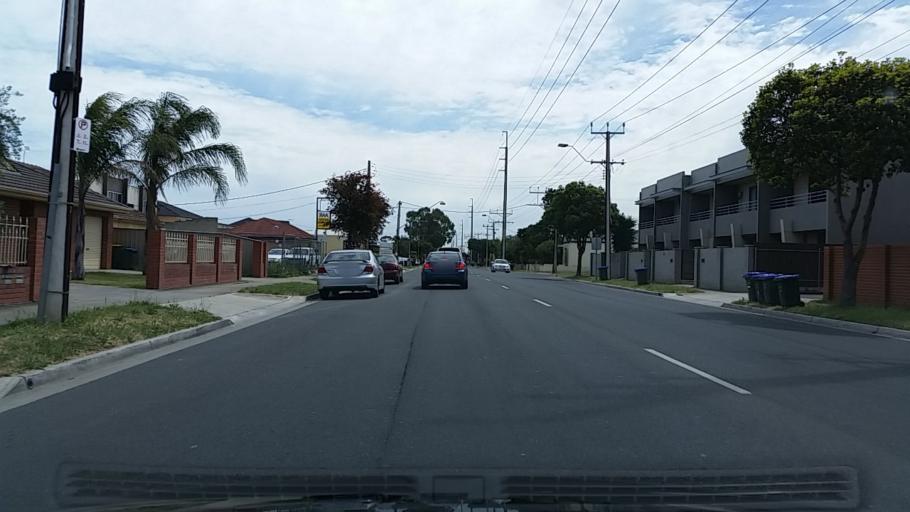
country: AU
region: South Australia
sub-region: Charles Sturt
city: Findon
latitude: -34.9024
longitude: 138.5323
